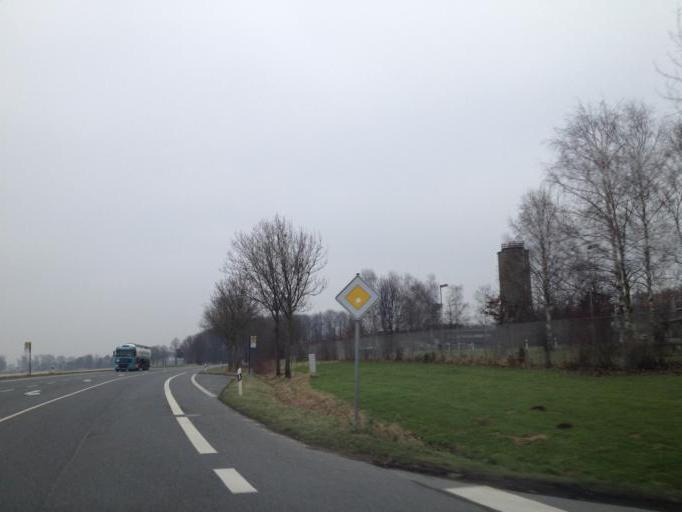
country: DE
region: North Rhine-Westphalia
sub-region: Regierungsbezirk Arnsberg
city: Mohnesee
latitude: 51.5269
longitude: 8.0933
